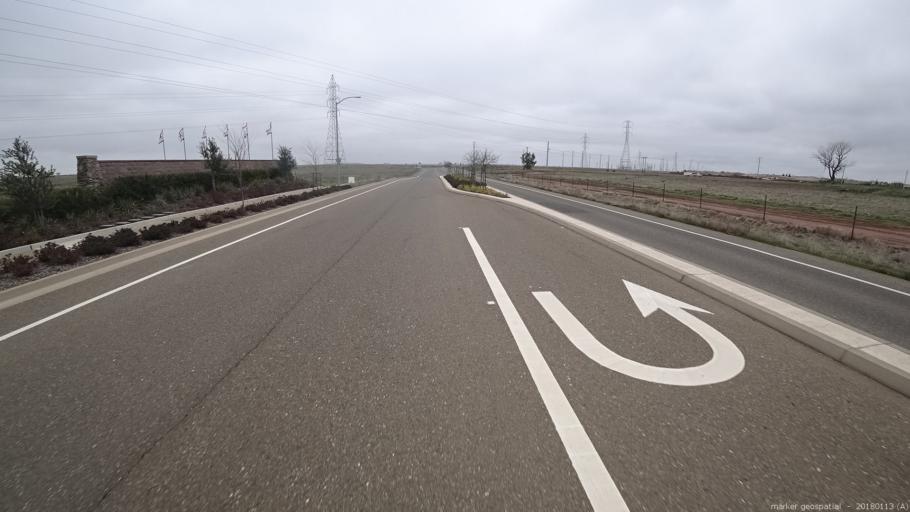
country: US
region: California
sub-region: Sacramento County
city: Gold River
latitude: 38.5612
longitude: -121.2022
